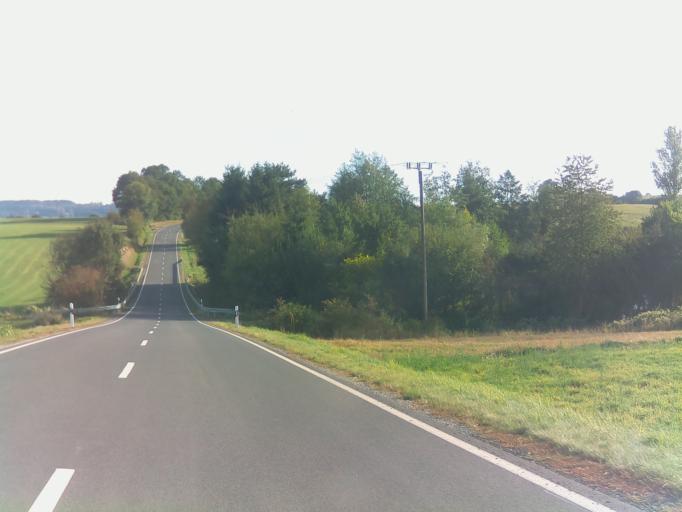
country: DE
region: Hesse
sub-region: Regierungsbezirk Kassel
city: Flieden
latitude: 50.4396
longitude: 9.5755
